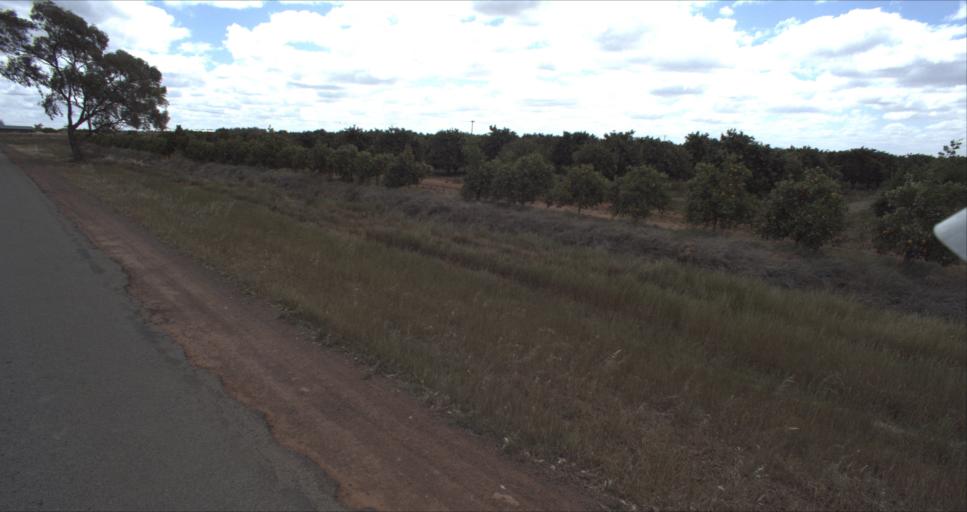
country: AU
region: New South Wales
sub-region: Leeton
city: Leeton
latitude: -34.5887
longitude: 146.3876
